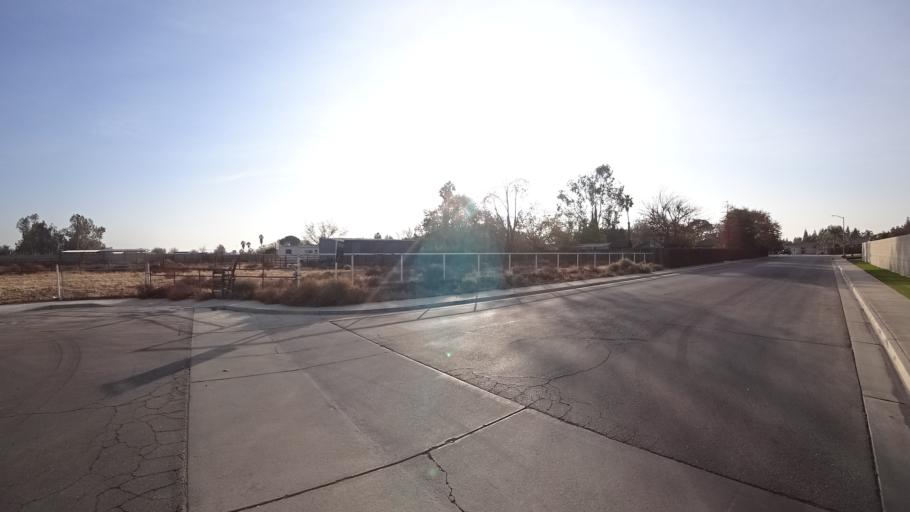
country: US
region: California
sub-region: Kern County
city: Greenacres
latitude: 35.3736
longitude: -119.1237
